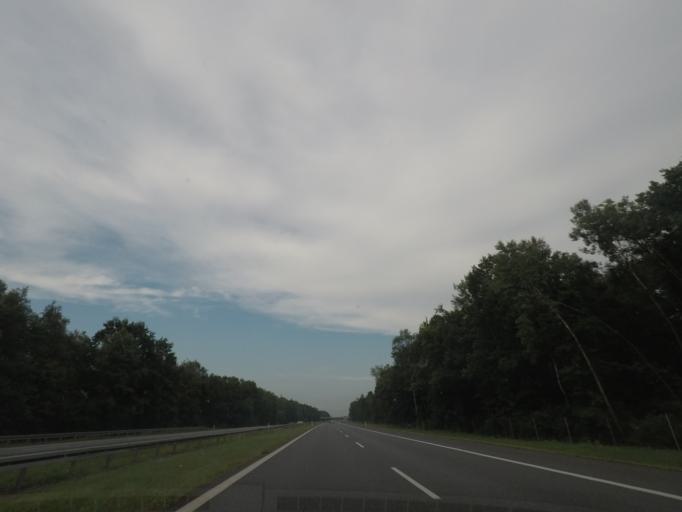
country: PL
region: Silesian Voivodeship
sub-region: Jaworzno
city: Jaworzno
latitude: 50.1498
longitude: 19.2790
